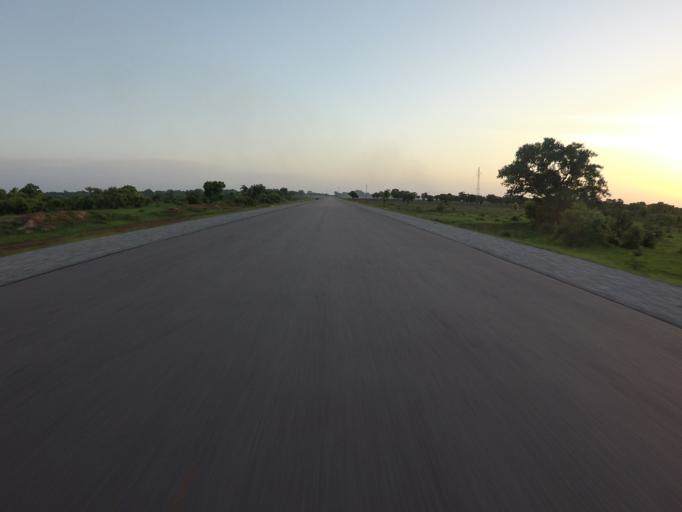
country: GH
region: Northern
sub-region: Yendi
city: Yendi
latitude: 9.9593
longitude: -0.1473
